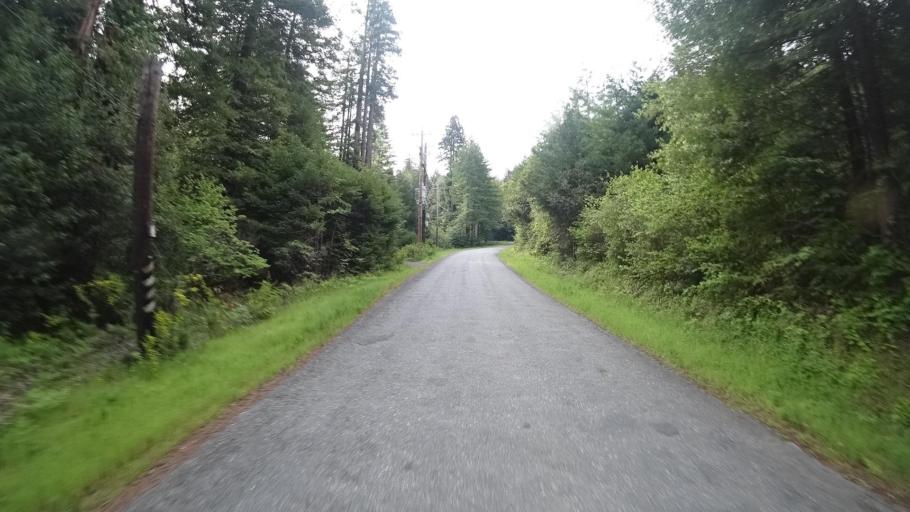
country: US
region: California
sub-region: Humboldt County
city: Redway
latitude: 40.3413
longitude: -123.9156
